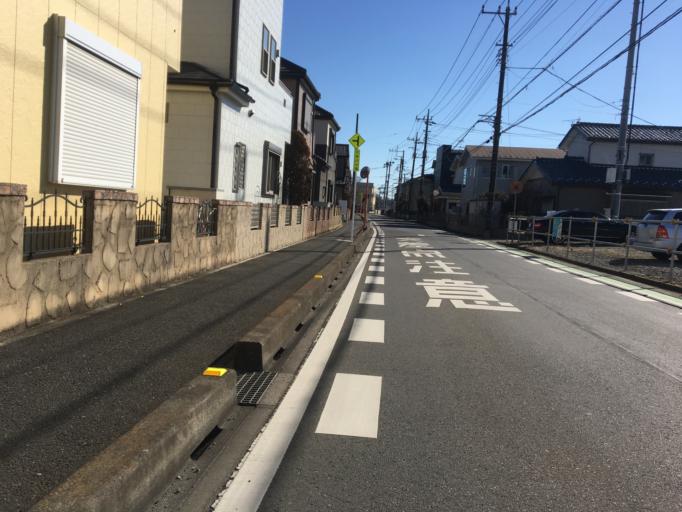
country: JP
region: Saitama
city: Oi
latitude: 35.8361
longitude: 139.5211
